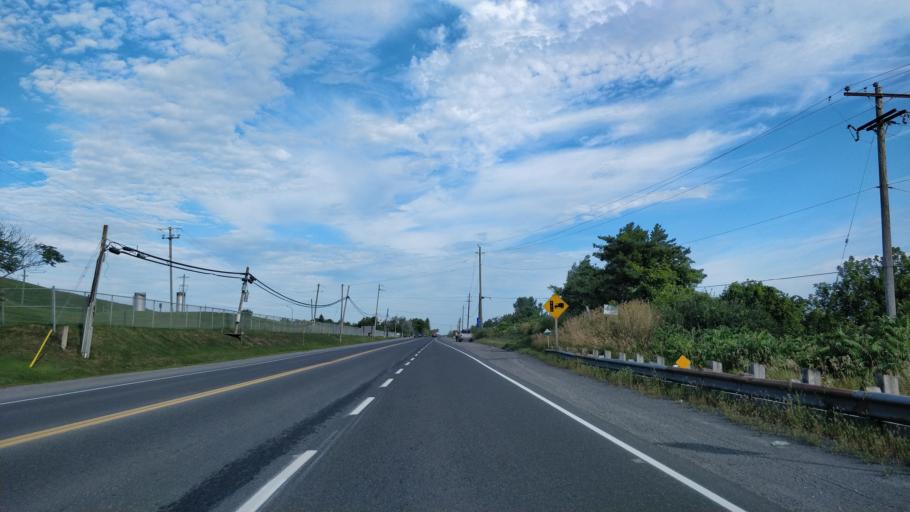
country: CA
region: Ontario
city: Bells Corners
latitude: 45.2833
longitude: -75.9598
